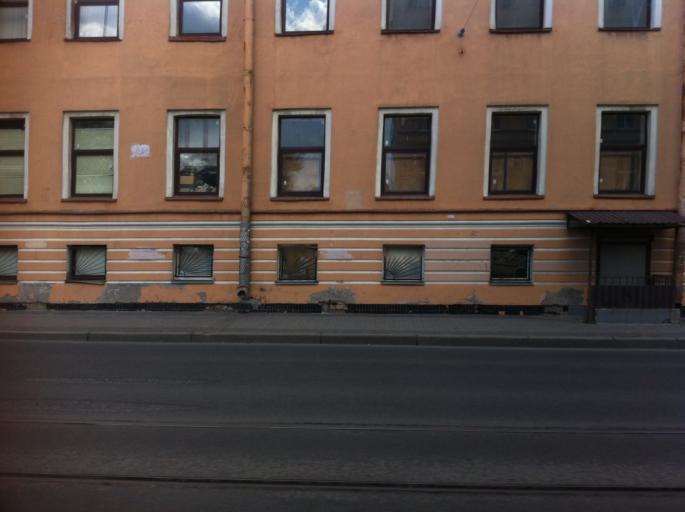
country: RU
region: St.-Petersburg
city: Admiralteisky
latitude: 59.9140
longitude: 30.2780
